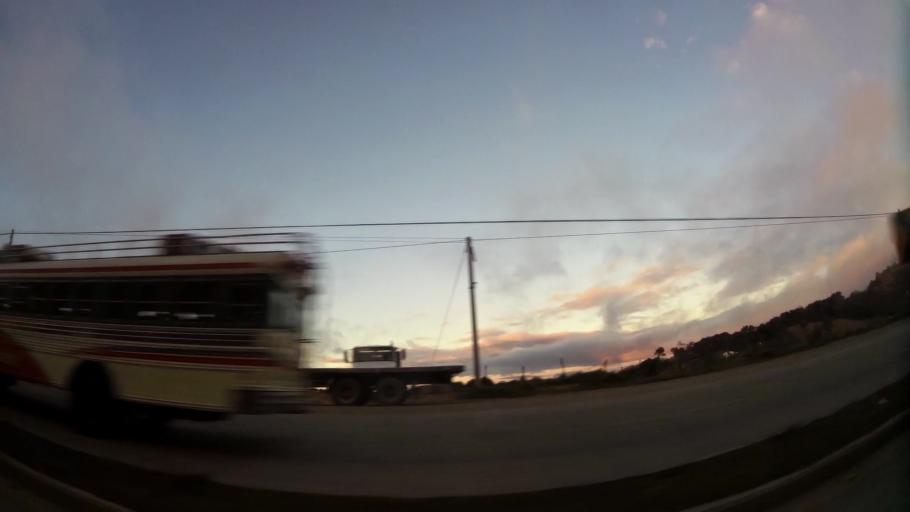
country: GT
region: Solola
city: Concepcion
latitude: 14.8373
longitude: -91.1161
